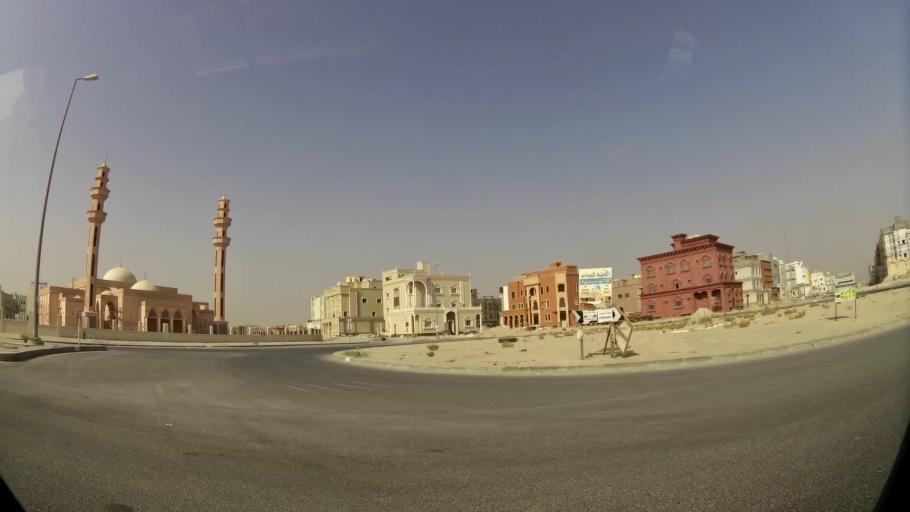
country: KW
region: Muhafazat al Jahra'
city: Al Jahra'
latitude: 29.3536
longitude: 47.7705
